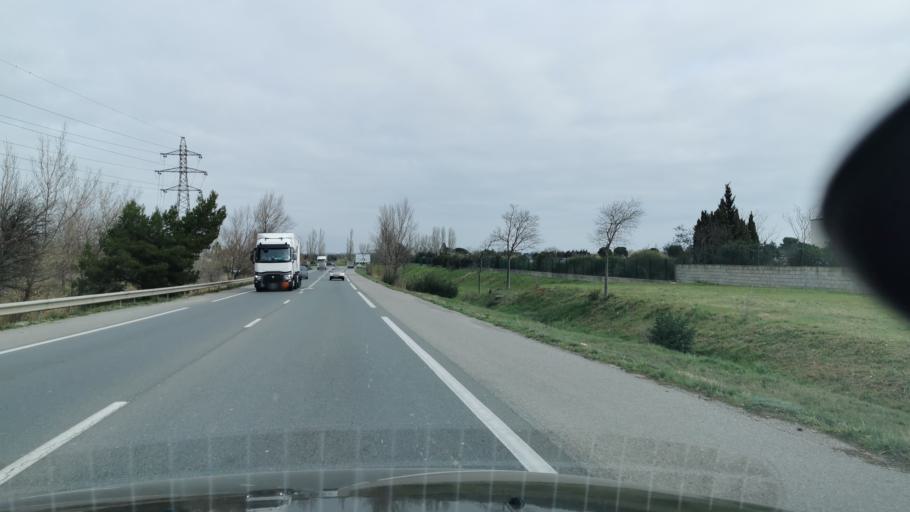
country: FR
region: Languedoc-Roussillon
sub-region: Departement de l'Aude
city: Narbonne
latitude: 43.1911
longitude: 2.9774
